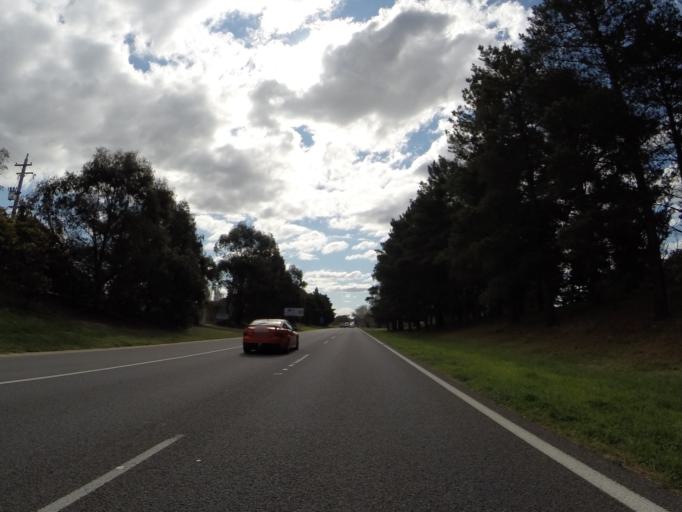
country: AU
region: Australian Capital Territory
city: Belconnen
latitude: -35.1972
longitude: 149.0893
